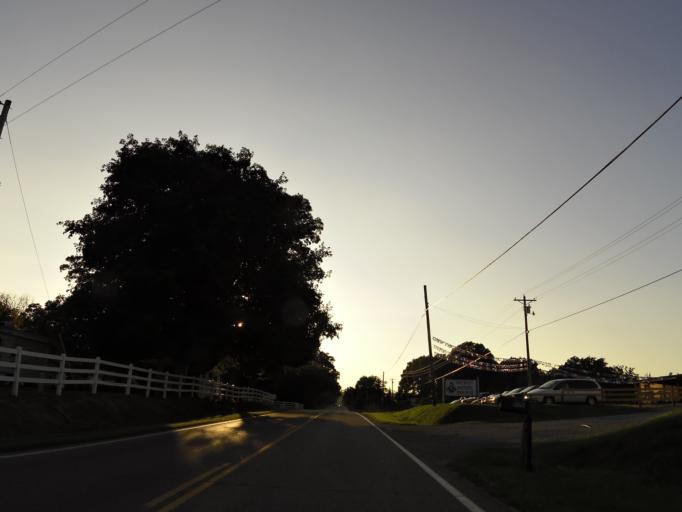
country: US
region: Tennessee
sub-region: Jefferson County
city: White Pine
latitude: 36.0326
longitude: -83.3233
